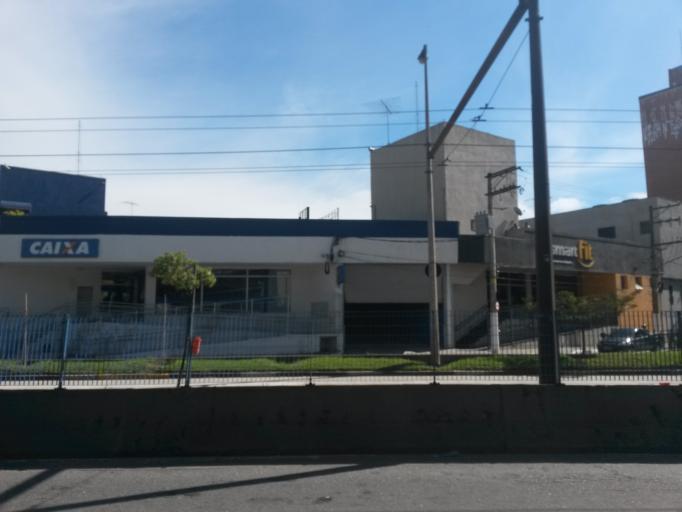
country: BR
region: Sao Paulo
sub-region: Sao Bernardo Do Campo
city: Sao Bernardo do Campo
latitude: -23.7004
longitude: -46.5523
